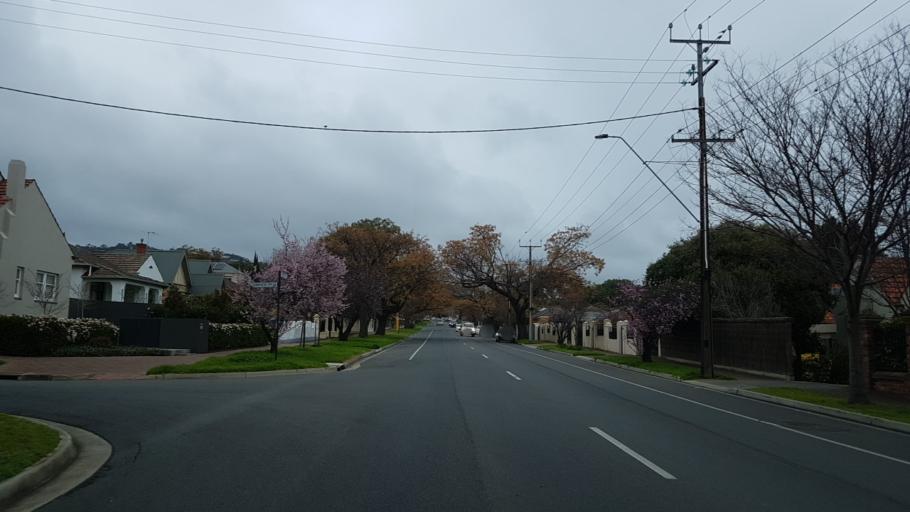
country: AU
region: South Australia
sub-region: Burnside
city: Tusmore
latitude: -34.9424
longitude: 138.6517
